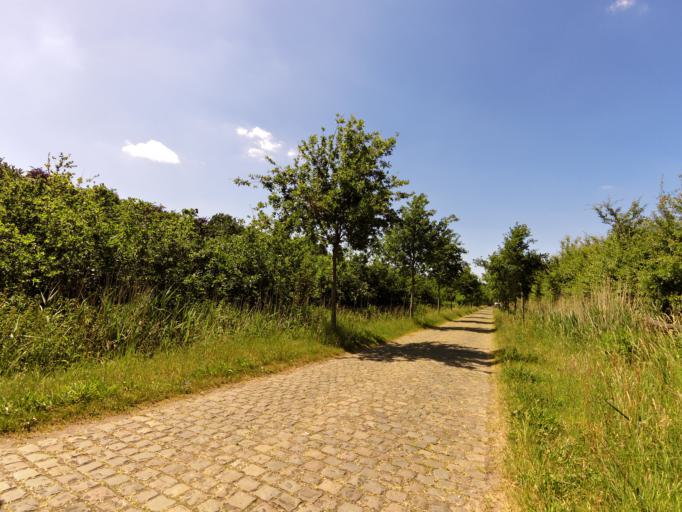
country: BE
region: Flanders
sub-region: Provincie West-Vlaanderen
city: Zedelgem
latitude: 51.1439
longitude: 3.1158
